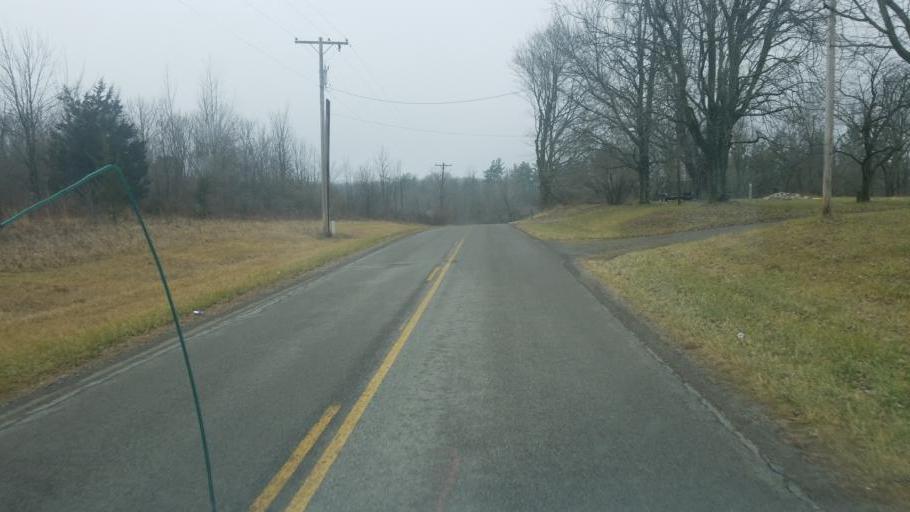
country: US
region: Ohio
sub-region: Champaign County
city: North Lewisburg
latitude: 40.3055
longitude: -83.5828
